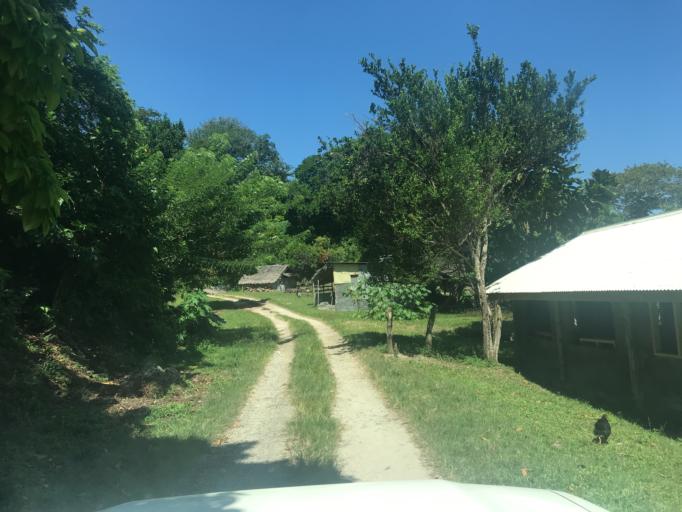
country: VU
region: Sanma
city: Luganville
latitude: -15.5943
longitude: 166.7796
